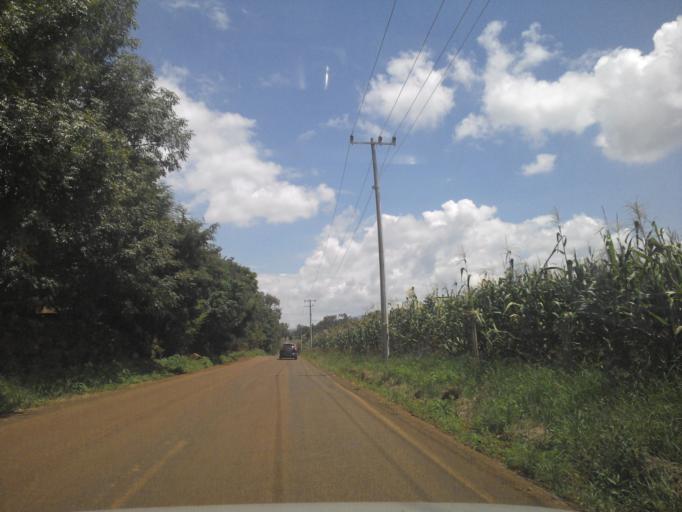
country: MX
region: Jalisco
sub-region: Atotonilco el Alto
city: Ojo de Agua de Moran
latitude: 20.6021
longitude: -102.4859
